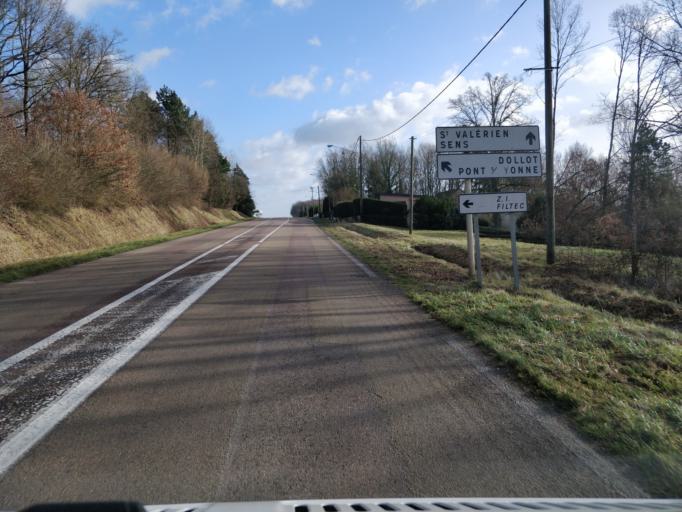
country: FR
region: Bourgogne
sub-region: Departement de l'Yonne
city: Cheroy
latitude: 48.1999
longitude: 3.0132
